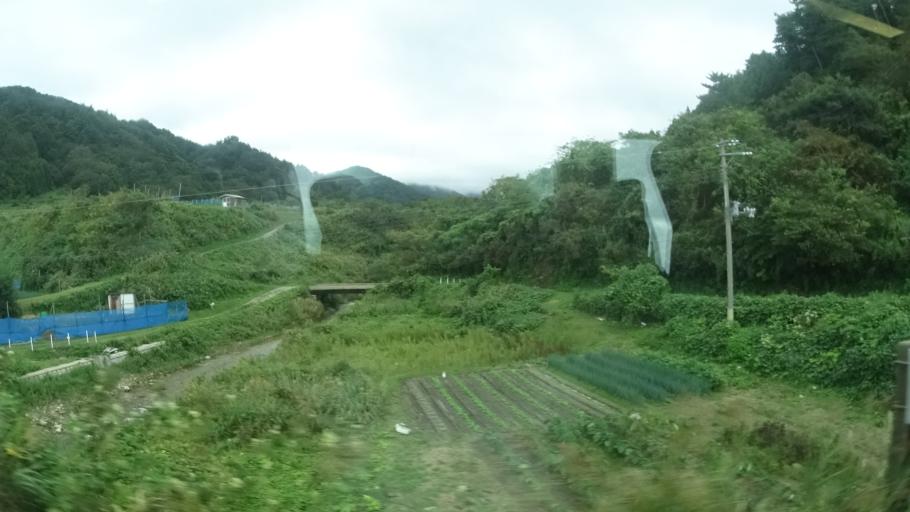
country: JP
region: Niigata
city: Murakami
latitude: 38.4140
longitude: 139.4685
